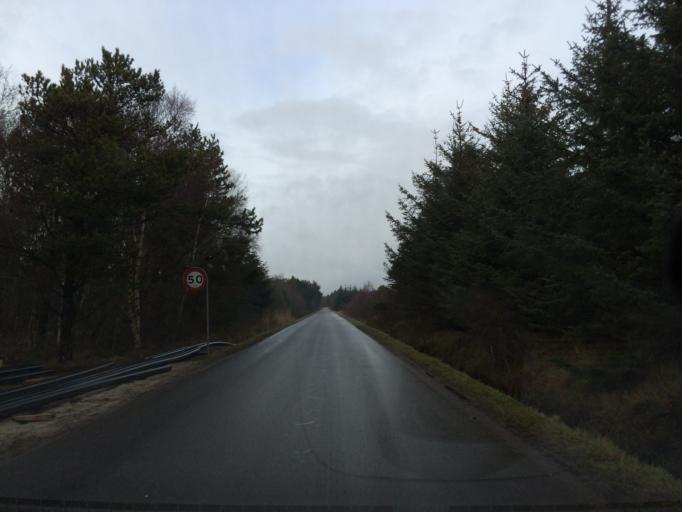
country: DK
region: Central Jutland
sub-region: Holstebro Kommune
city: Ulfborg
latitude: 56.2650
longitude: 8.1513
